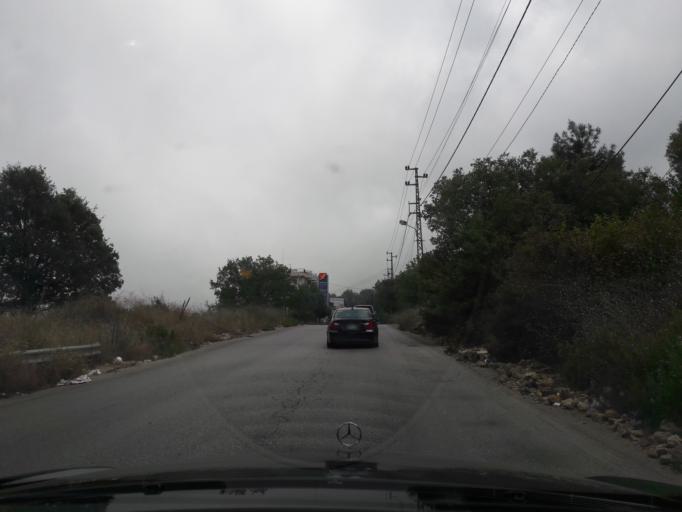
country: LB
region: Mont-Liban
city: Djounie
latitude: 33.9140
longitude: 35.6879
